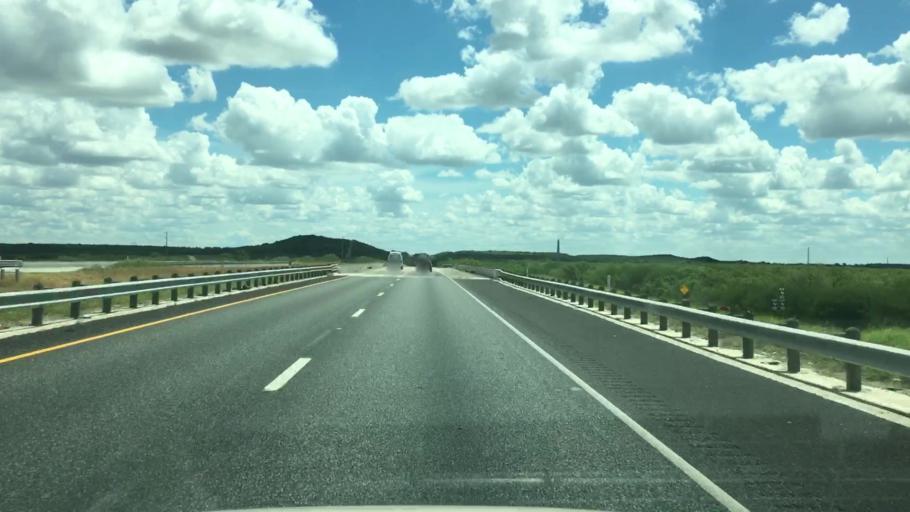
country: US
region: Texas
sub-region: Live Oak County
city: Three Rivers
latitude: 28.7344
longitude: -98.2897
